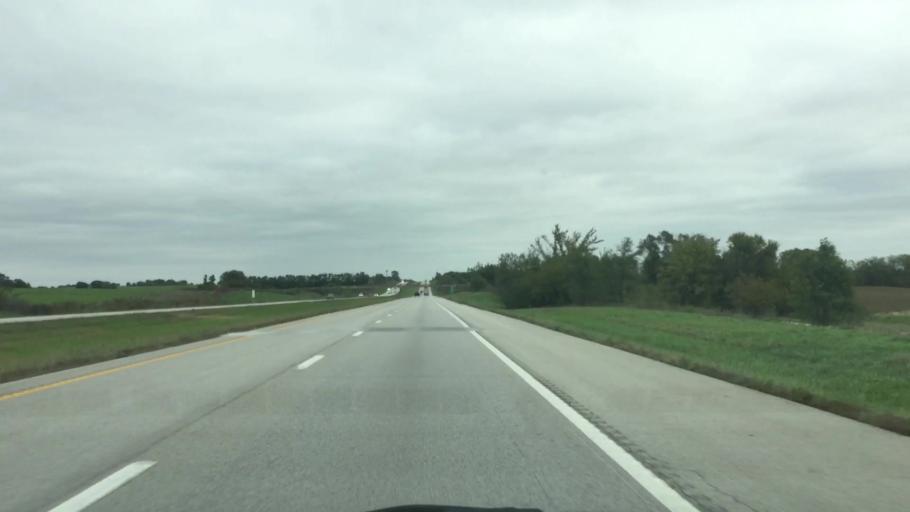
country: US
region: Missouri
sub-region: Clinton County
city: Cameron
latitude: 39.7986
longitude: -94.2010
